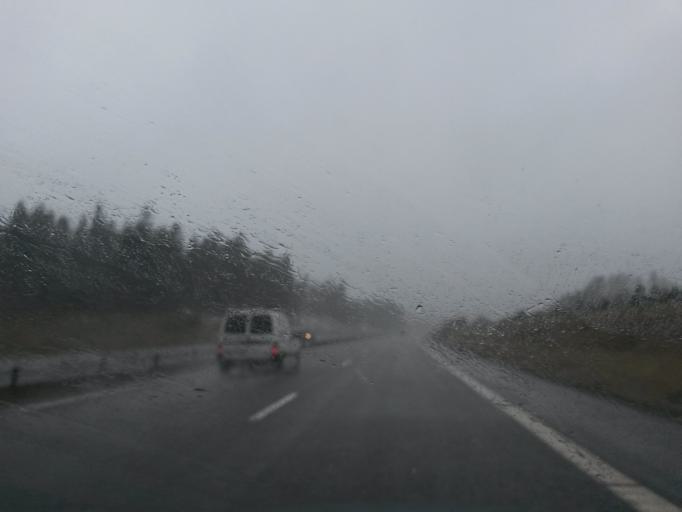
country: SE
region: Vaestra Goetaland
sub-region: Trollhattan
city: Sjuntorp
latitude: 58.3267
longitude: 12.1492
